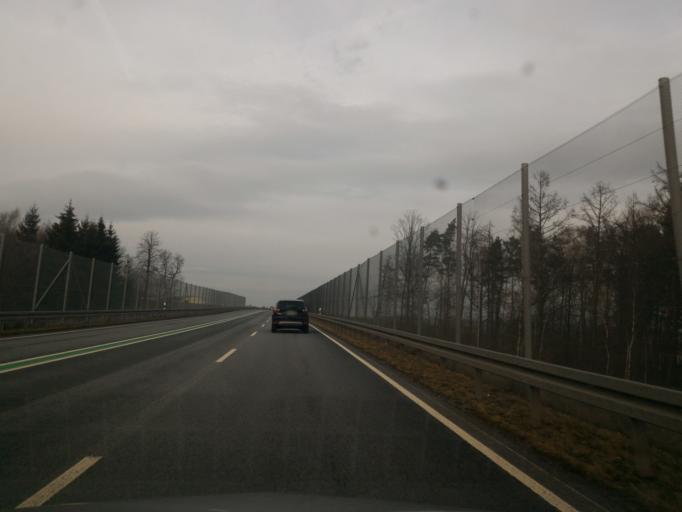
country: DE
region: Saxony
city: Eibau
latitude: 51.0129
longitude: 14.6847
